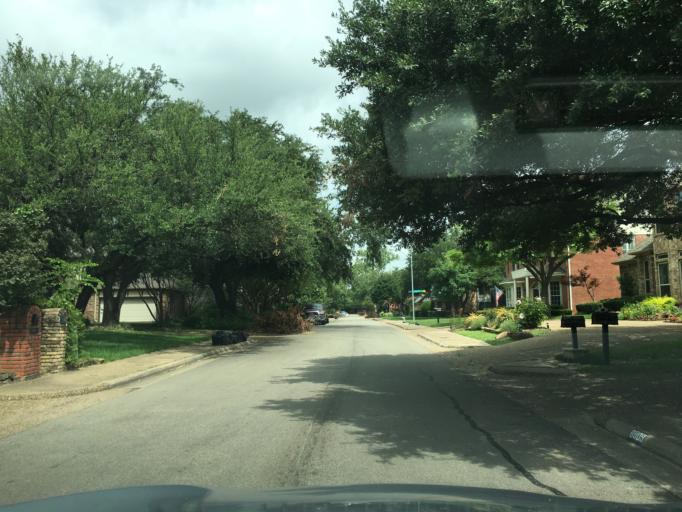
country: US
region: Texas
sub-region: Dallas County
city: University Park
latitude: 32.8794
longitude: -96.7437
